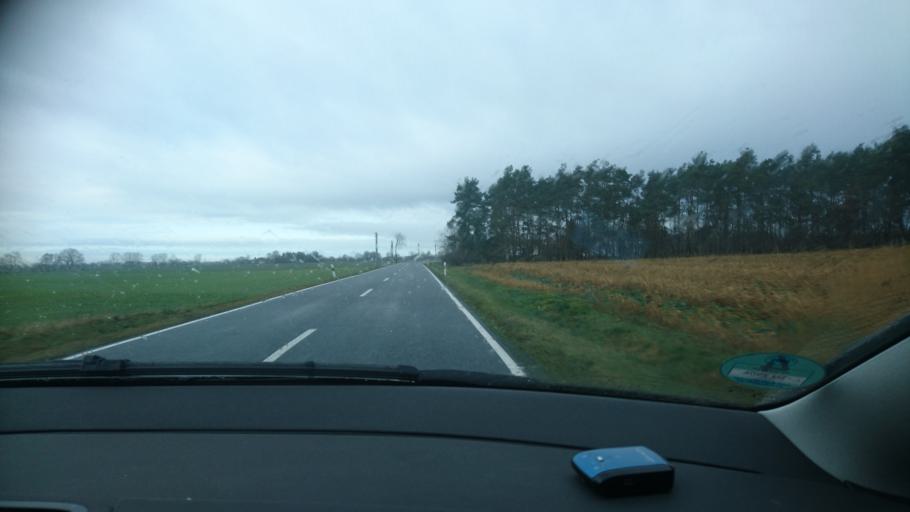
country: DE
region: Saxony
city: Laussig
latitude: 51.5816
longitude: 12.6326
